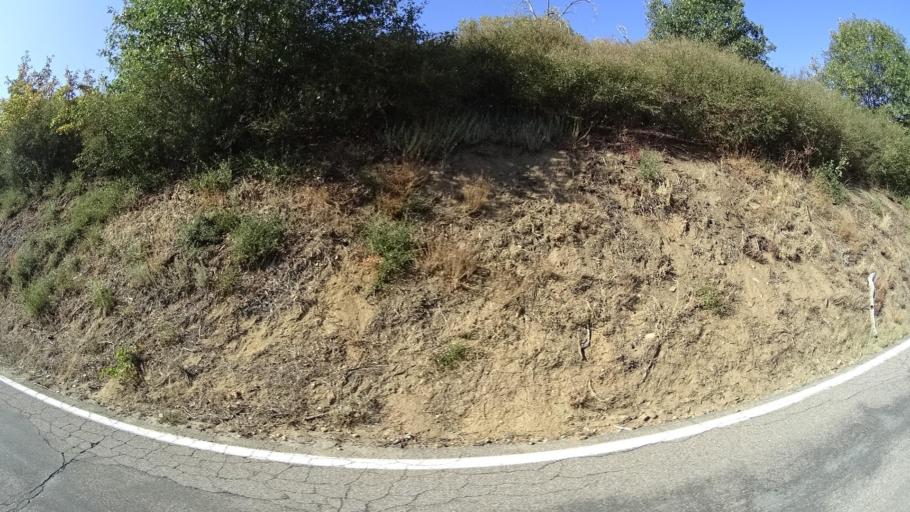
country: US
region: California
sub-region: San Diego County
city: Pine Valley
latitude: 32.9227
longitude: -116.4753
